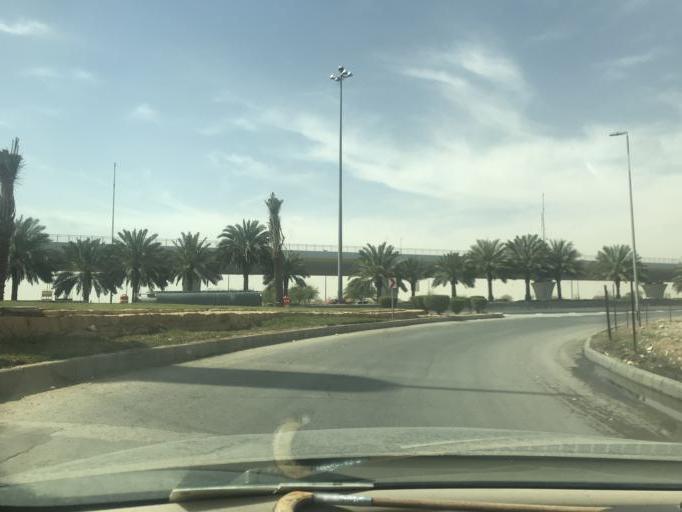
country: SA
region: Ar Riyad
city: Riyadh
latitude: 24.8221
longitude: 46.7180
